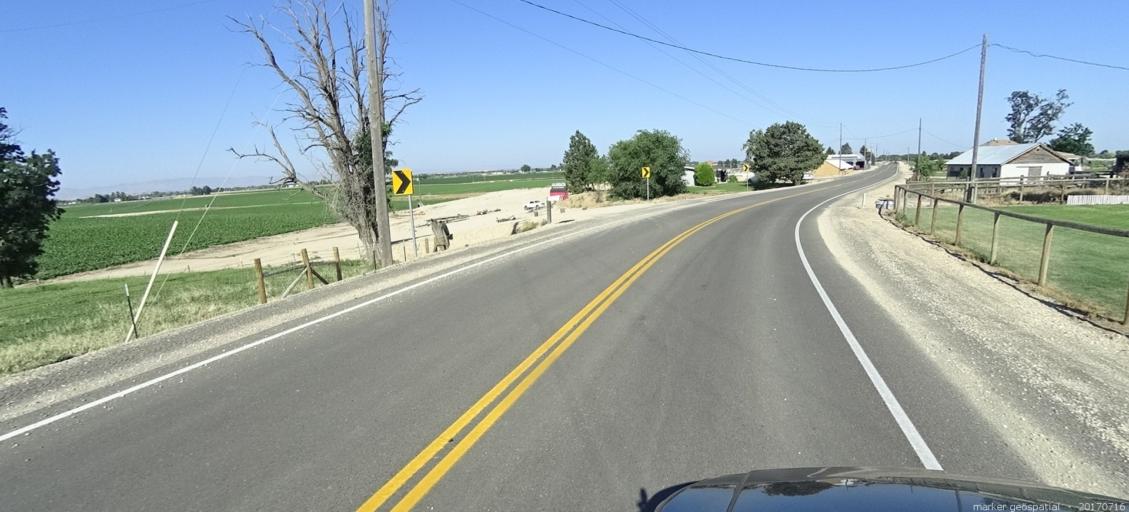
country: US
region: Idaho
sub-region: Canyon County
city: Nampa
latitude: 43.5468
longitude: -116.4834
